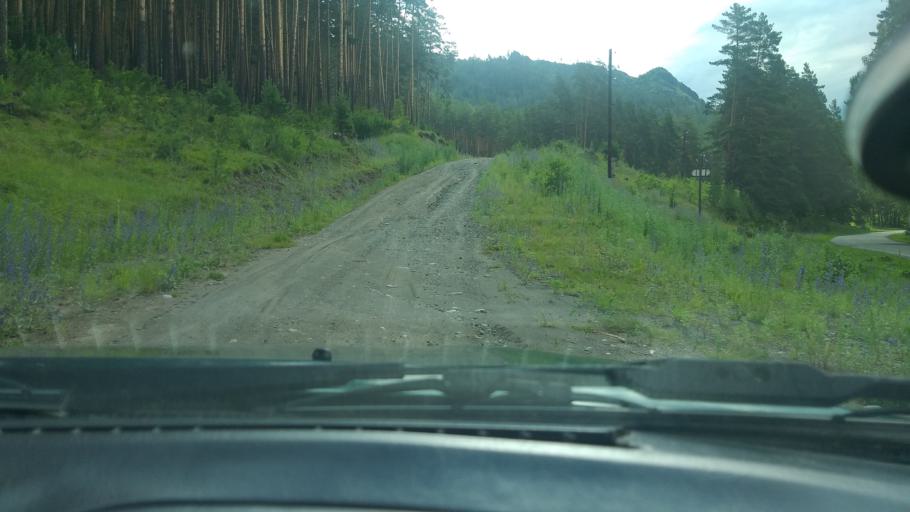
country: RU
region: Altay
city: Chemal
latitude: 51.3910
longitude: 86.0486
